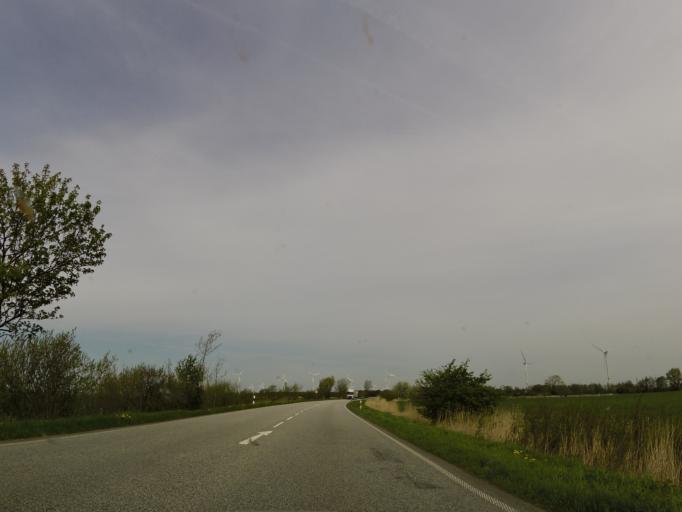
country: DE
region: Schleswig-Holstein
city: Stelle-Wittenwurth
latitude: 54.2355
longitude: 9.0367
